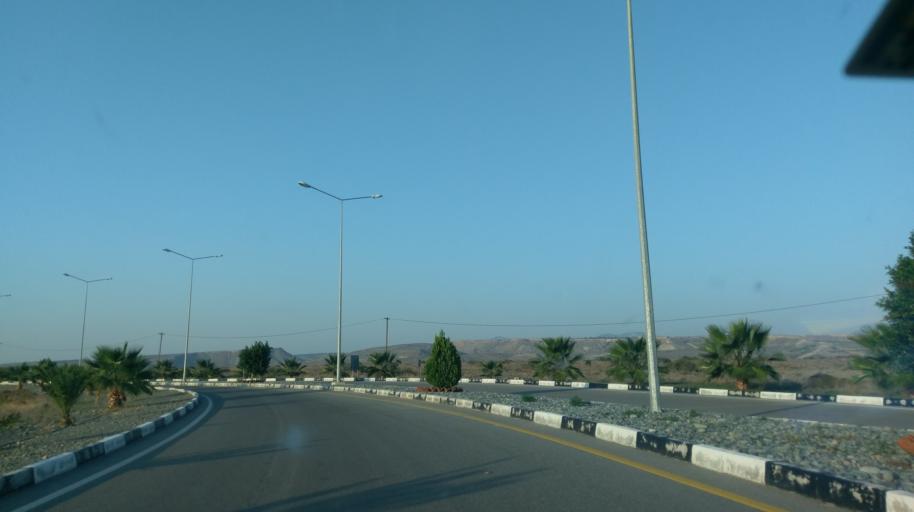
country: CY
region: Lefkosia
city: Astromeritis
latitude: 35.1964
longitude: 33.0642
